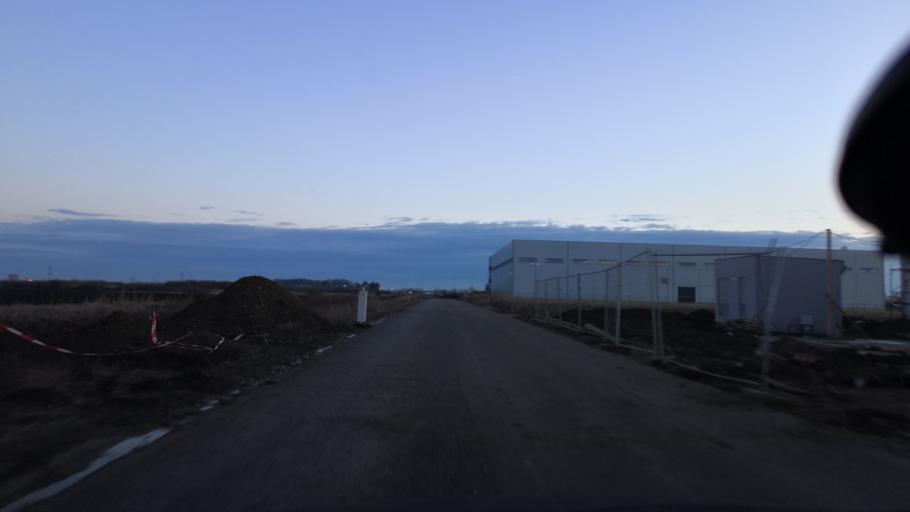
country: RS
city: Simanovci
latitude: 44.8858
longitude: 20.1127
